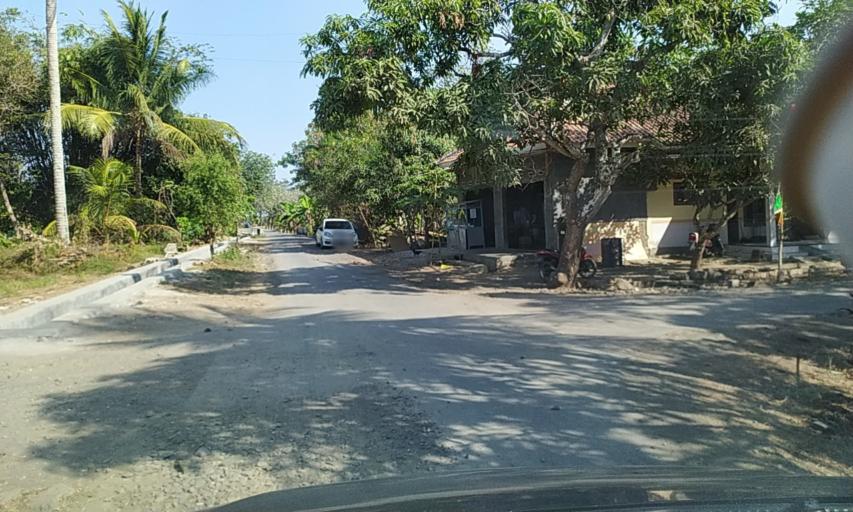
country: ID
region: Central Java
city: Dukuhtengah
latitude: -7.5141
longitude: 108.8028
